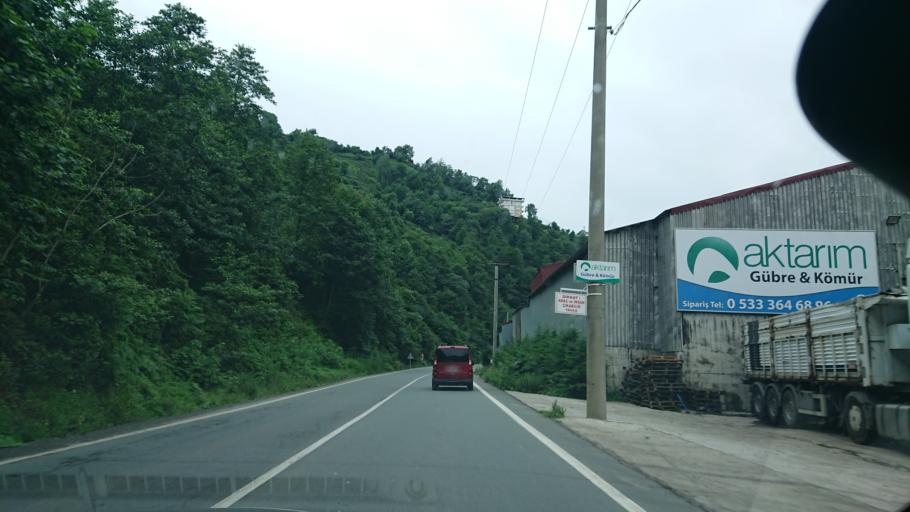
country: TR
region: Rize
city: Gundogdu
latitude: 41.0337
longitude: 40.5808
